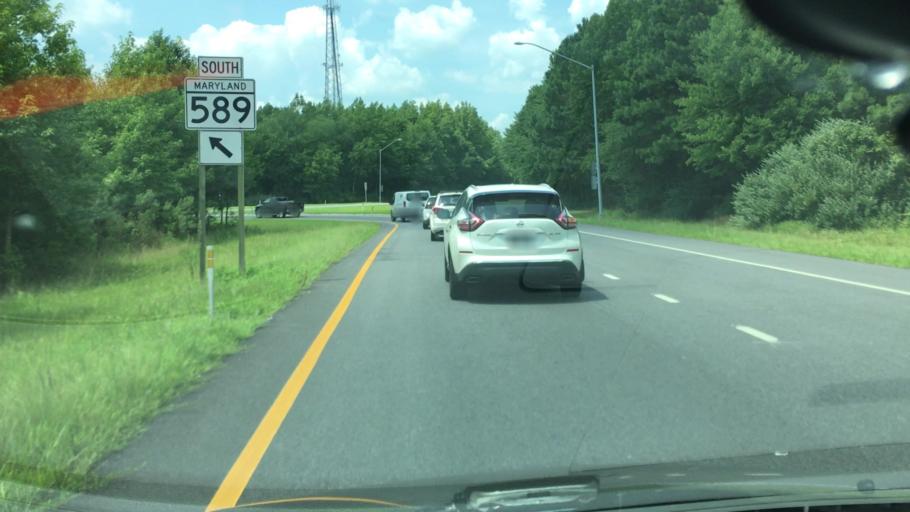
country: US
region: Maryland
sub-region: Worcester County
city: Ocean Pines
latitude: 38.3814
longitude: -75.1707
